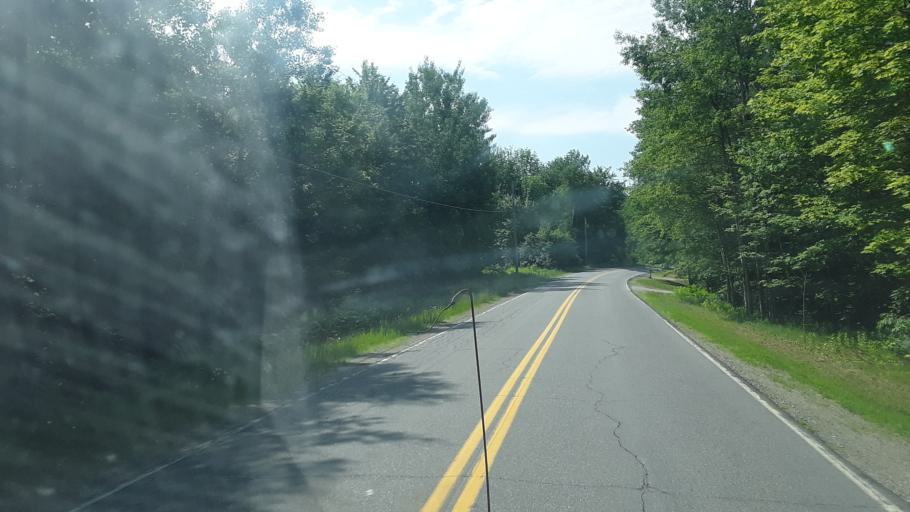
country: US
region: Maine
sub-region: Waldo County
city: Swanville
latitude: 44.5592
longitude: -68.9537
